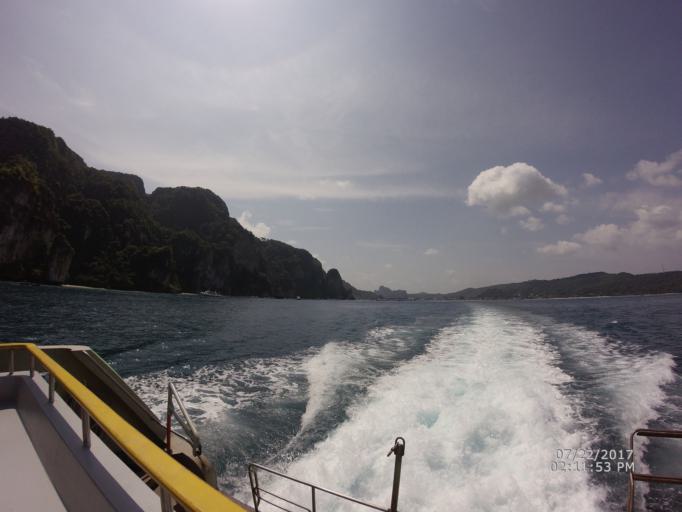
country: TH
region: Krabi
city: Saladan
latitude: 7.7200
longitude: 98.7723
